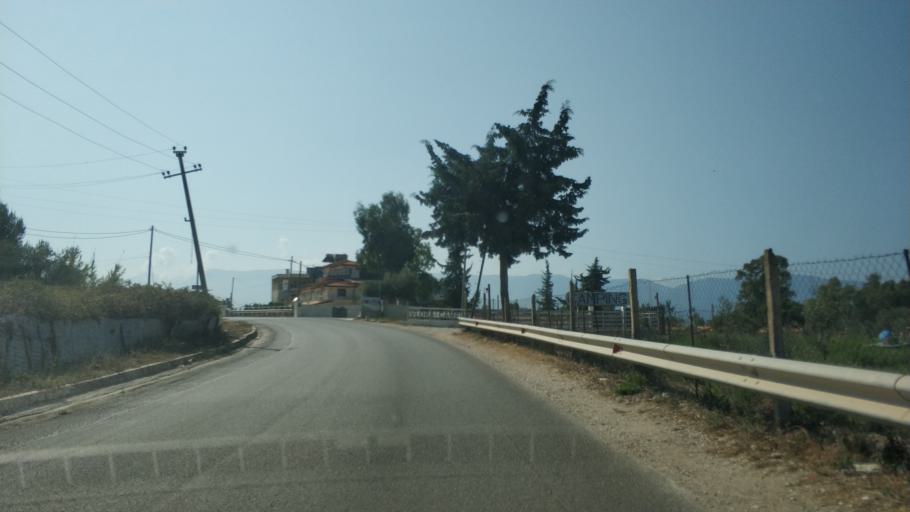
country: AL
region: Vlore
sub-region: Rrethi i Vlores
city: Orikum
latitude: 40.3780
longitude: 19.4810
